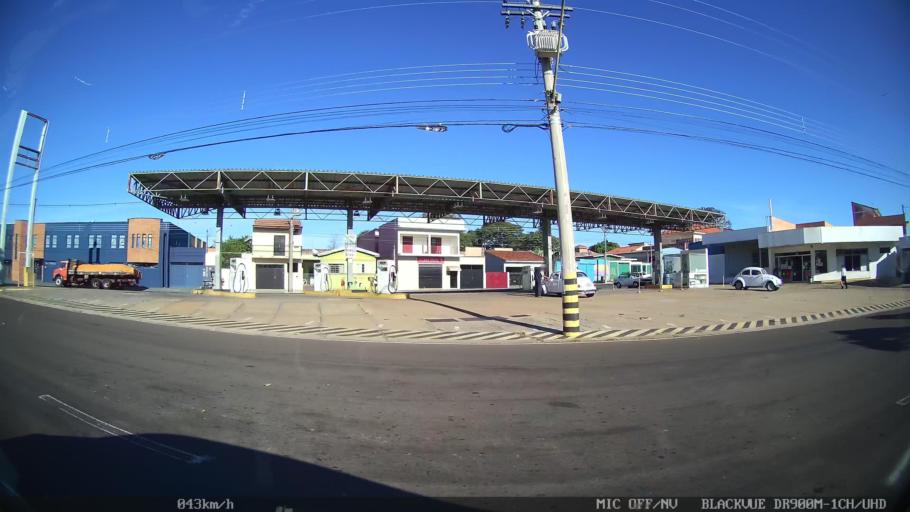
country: BR
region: Sao Paulo
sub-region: Franca
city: Franca
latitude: -20.5665
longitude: -47.3940
